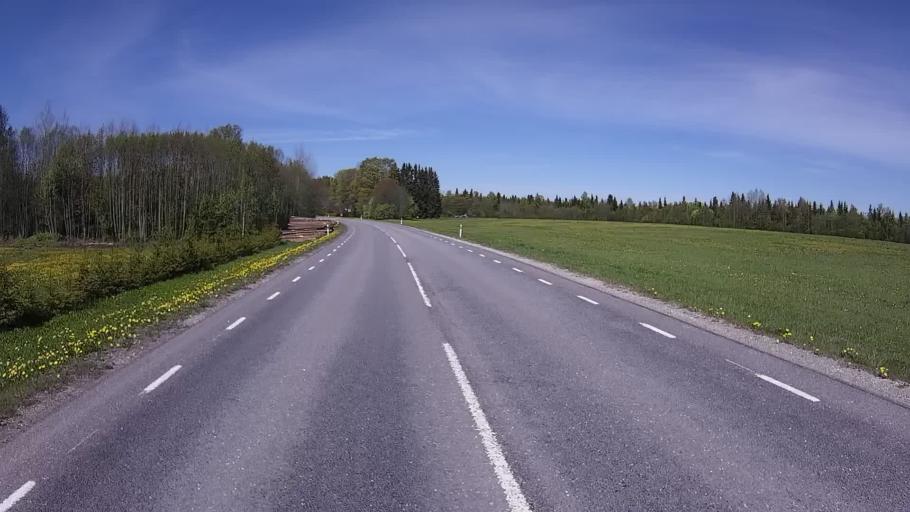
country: EE
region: Raplamaa
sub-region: Kehtna vald
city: Kehtna
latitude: 59.0503
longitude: 25.0229
